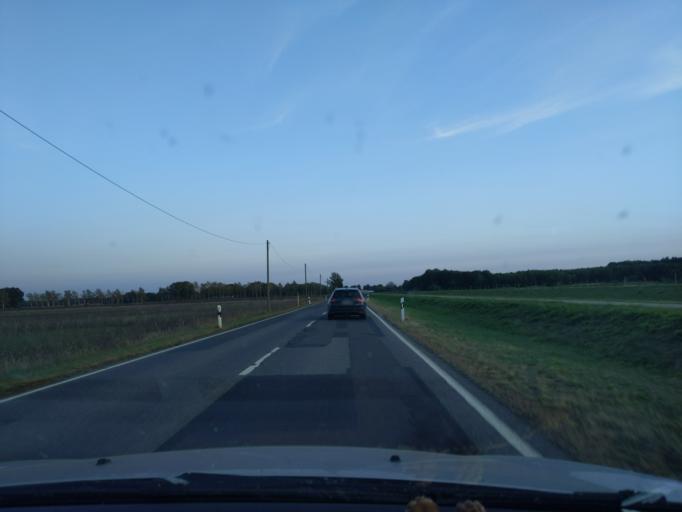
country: DE
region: Saxony
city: Hoyerswerda
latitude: 51.4729
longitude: 14.1998
